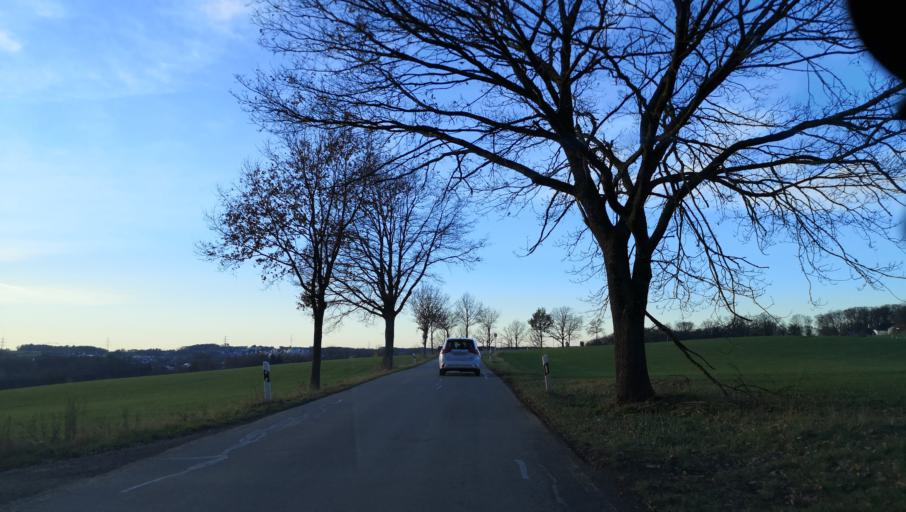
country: DE
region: North Rhine-Westphalia
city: Huckeswagen
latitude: 51.1433
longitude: 7.3622
